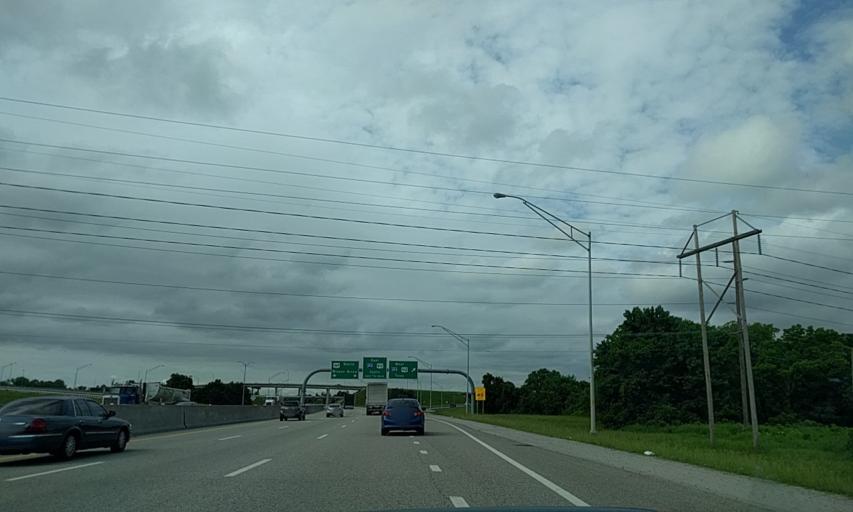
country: US
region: Oklahoma
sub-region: Tulsa County
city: Owasso
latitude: 36.1704
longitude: -95.8602
